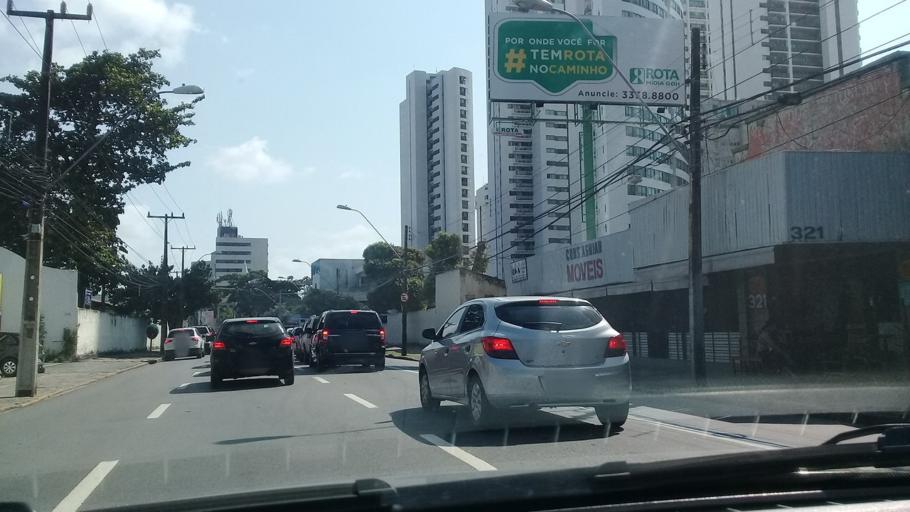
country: BR
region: Pernambuco
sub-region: Recife
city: Recife
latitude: -8.0937
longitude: -34.8841
